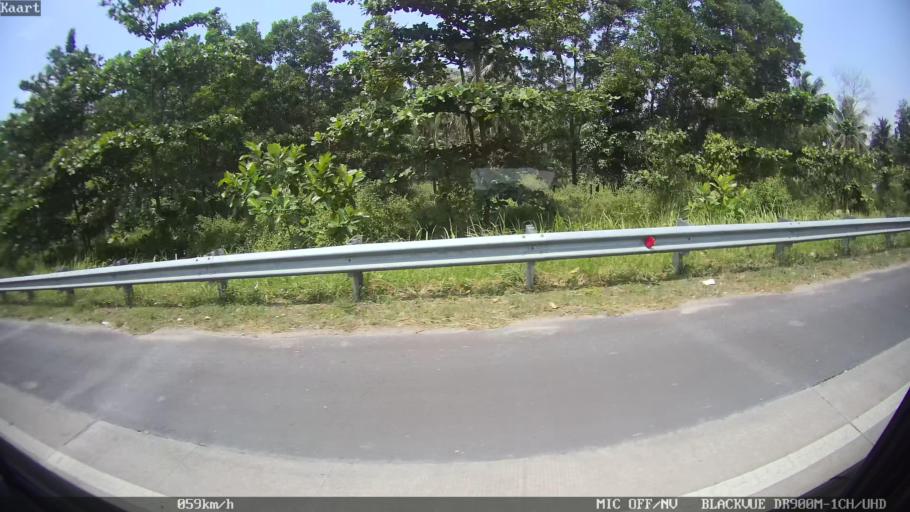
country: ID
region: Lampung
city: Kedaton
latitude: -5.3822
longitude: 105.3343
